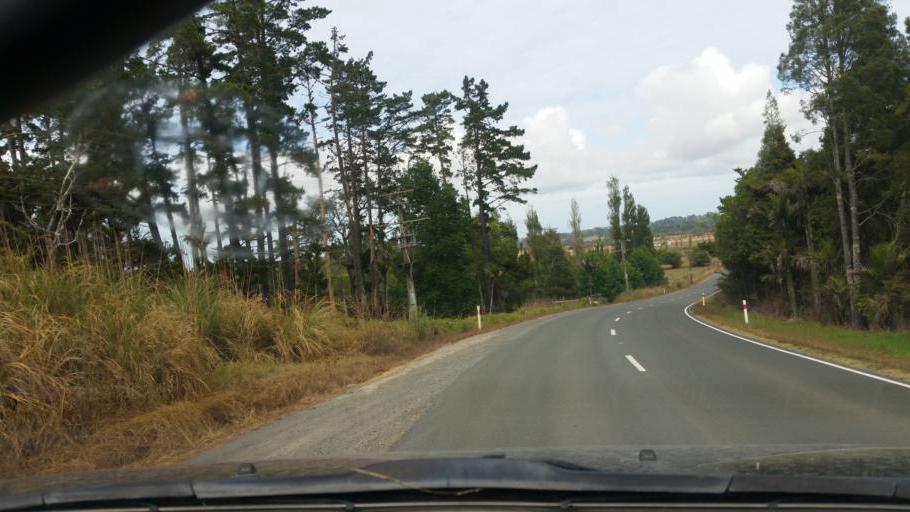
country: NZ
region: Northland
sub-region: Kaipara District
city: Dargaville
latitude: -35.9501
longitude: 173.9014
